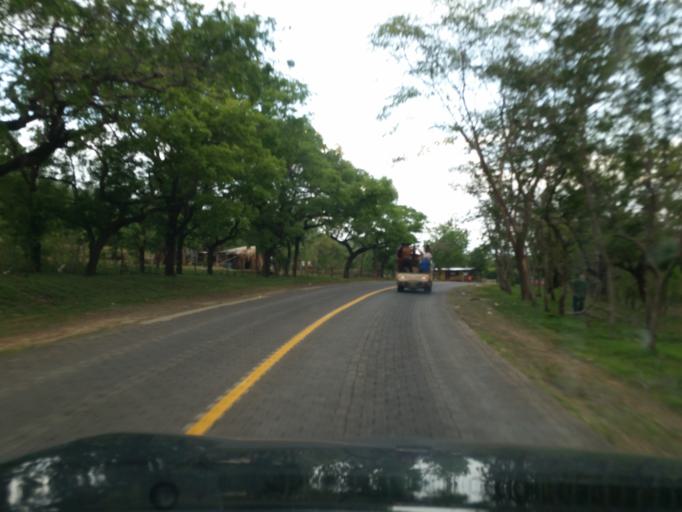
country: NI
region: Managua
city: Carlos Fonseca Amador
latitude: 12.0733
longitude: -86.4978
